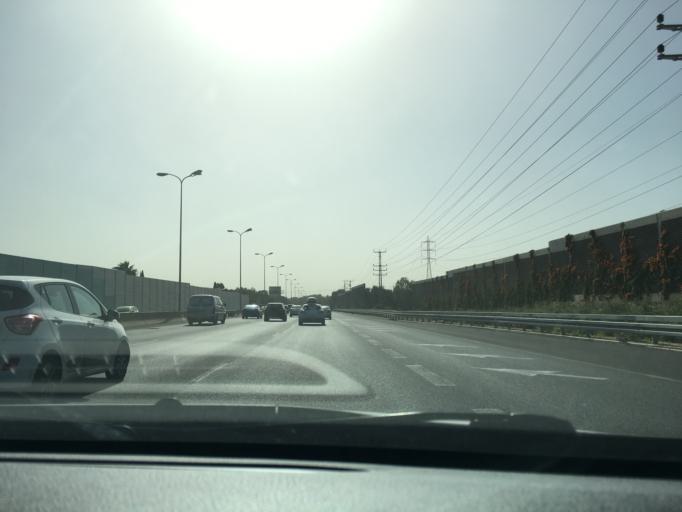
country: IL
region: Central District
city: Hod HaSharon
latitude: 32.1651
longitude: 34.8797
